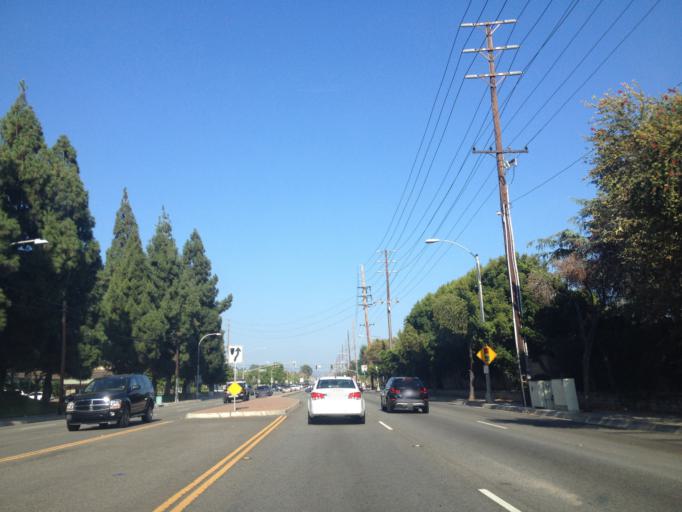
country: US
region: California
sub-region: Orange County
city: Brea
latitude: 33.9173
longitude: -117.9177
